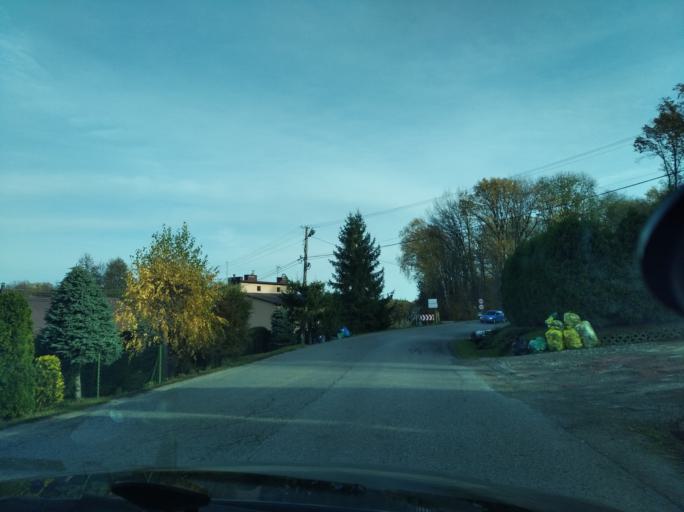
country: PL
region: Subcarpathian Voivodeship
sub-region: Powiat rzeszowski
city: Krasne
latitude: 50.0051
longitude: 22.0856
